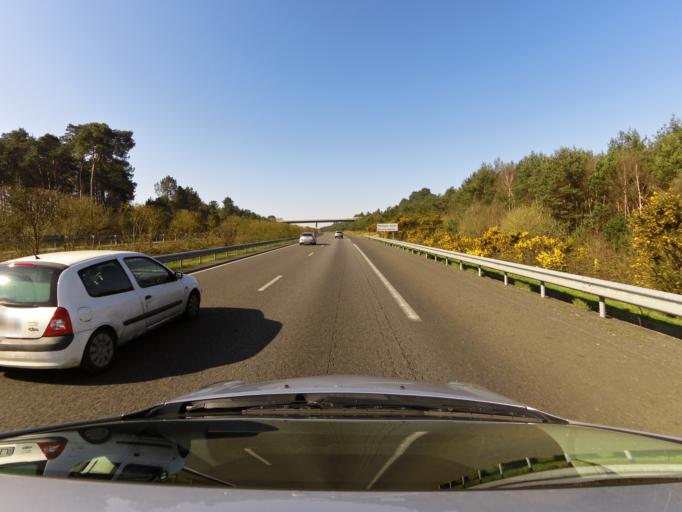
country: FR
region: Brittany
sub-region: Departement d'Ille-et-Vilaine
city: Gosne
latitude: 48.2352
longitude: -1.4798
